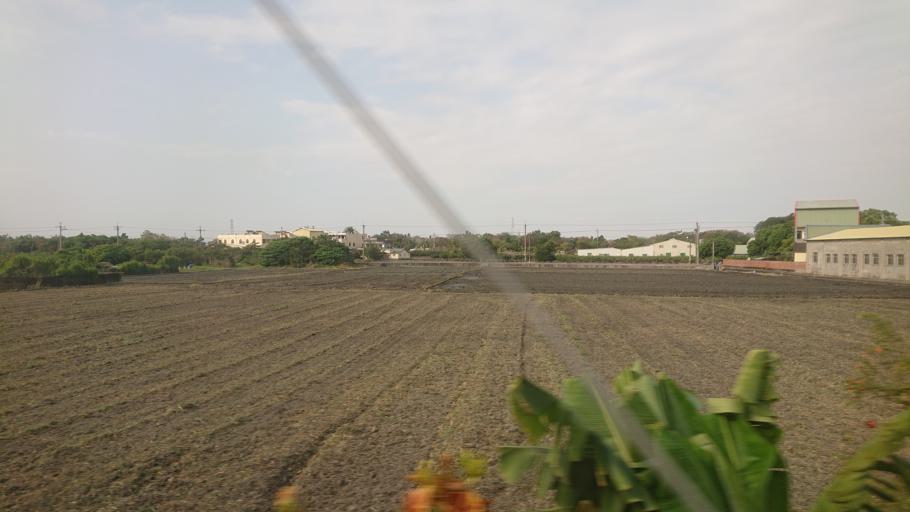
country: TW
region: Taiwan
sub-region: Nantou
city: Nantou
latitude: 23.8997
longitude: 120.5795
